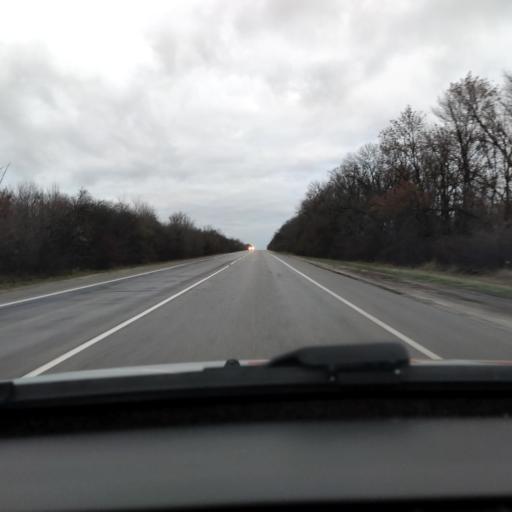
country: RU
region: Lipetsk
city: Khlevnoye
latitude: 52.3225
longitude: 39.1694
